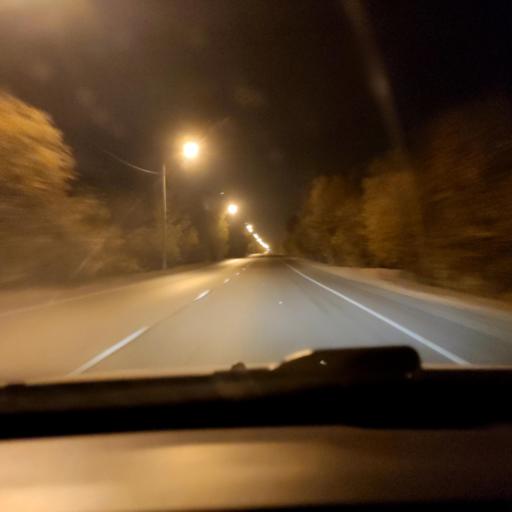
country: RU
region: Voronezj
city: Shilovo
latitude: 51.5757
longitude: 39.1466
